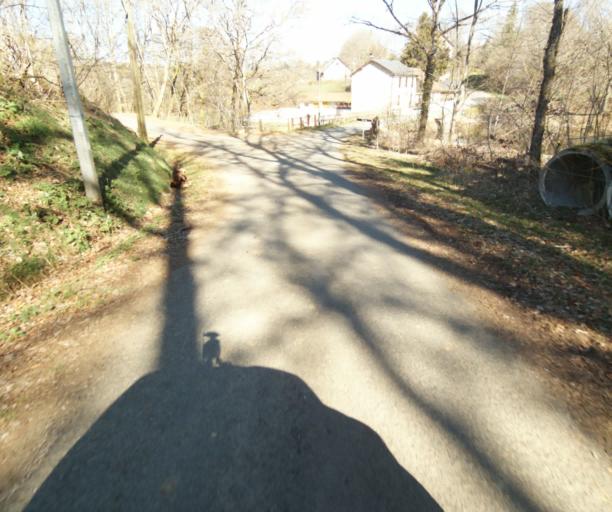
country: FR
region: Limousin
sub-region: Departement de la Correze
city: Chamboulive
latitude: 45.4170
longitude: 1.7211
